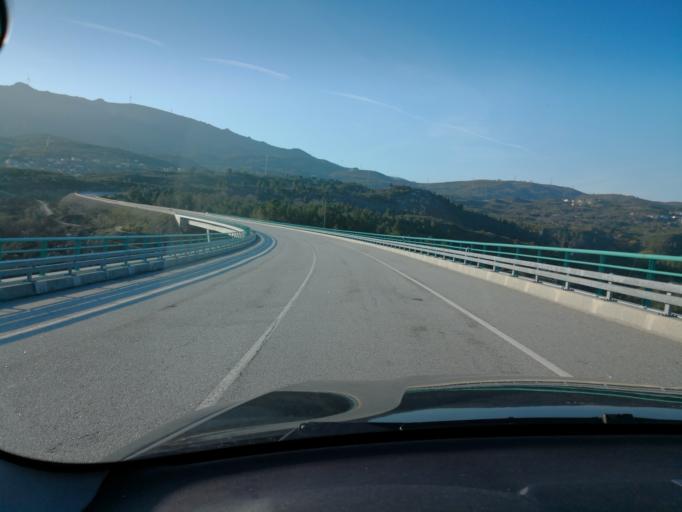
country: PT
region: Vila Real
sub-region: Vila Real
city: Vila Real
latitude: 41.3648
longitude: -7.7084
